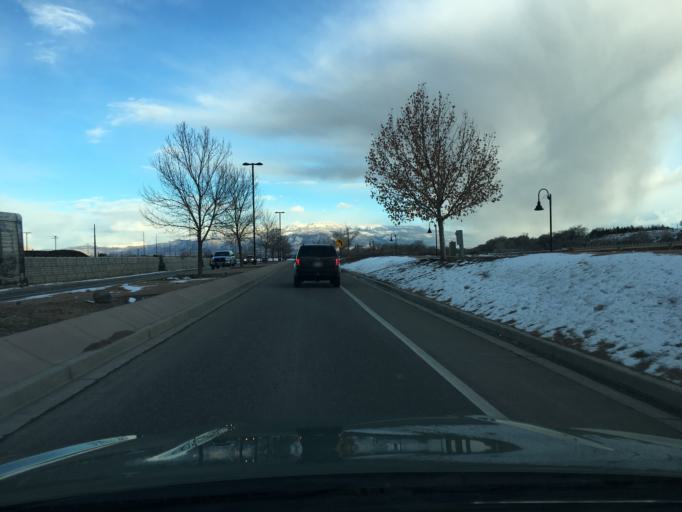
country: US
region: Colorado
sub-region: Mesa County
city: Grand Junction
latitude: 39.0560
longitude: -108.5504
